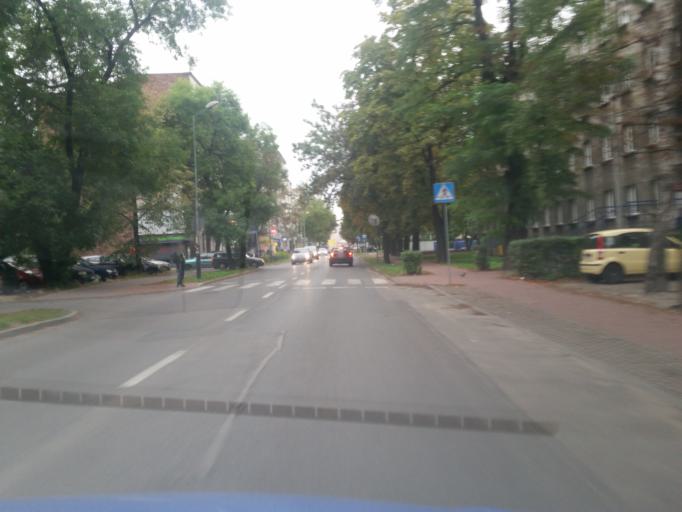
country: PL
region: Silesian Voivodeship
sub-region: Sosnowiec
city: Sosnowiec
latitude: 50.2708
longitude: 19.1278
